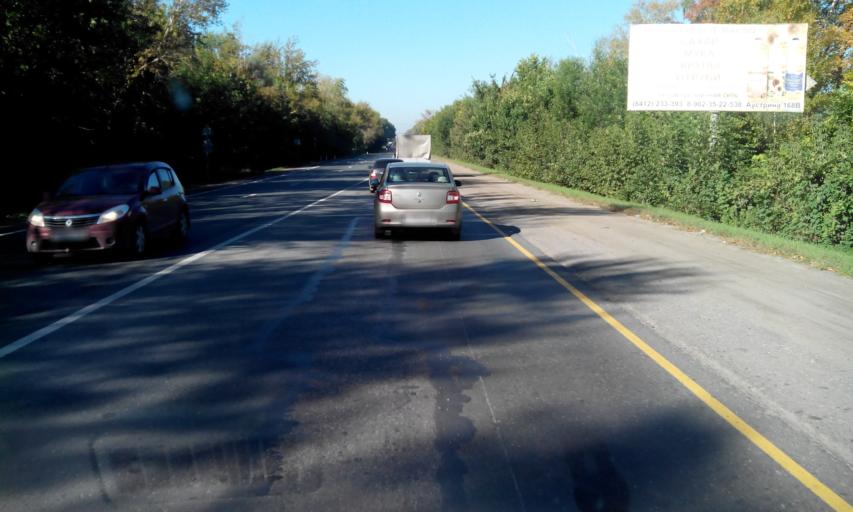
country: RU
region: Penza
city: Chemodanovka
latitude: 53.2215
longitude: 45.2237
